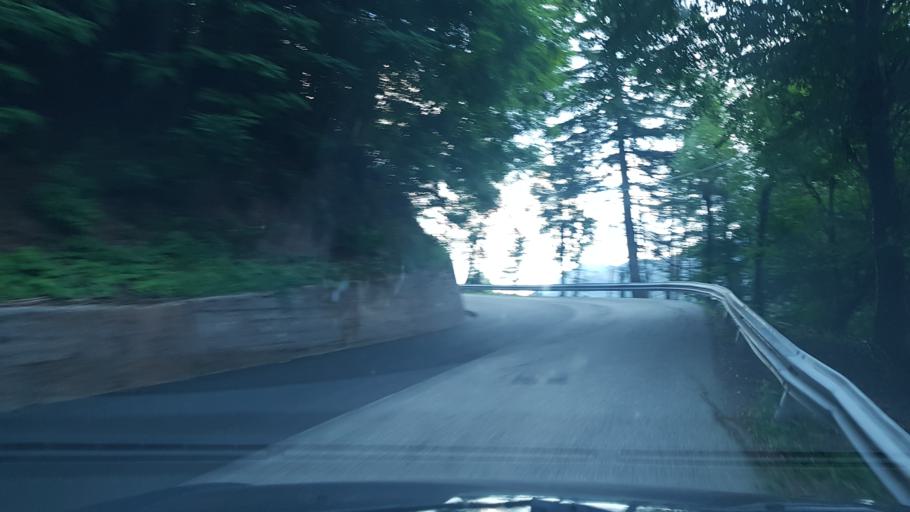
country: IT
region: Friuli Venezia Giulia
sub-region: Provincia di Udine
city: Forni Avoltri
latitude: 46.5859
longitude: 12.7836
